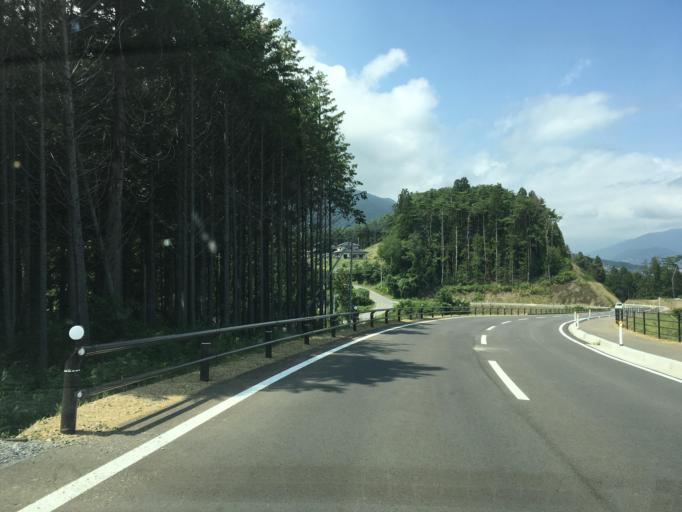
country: JP
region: Iwate
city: Ofunato
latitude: 39.0136
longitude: 141.7103
